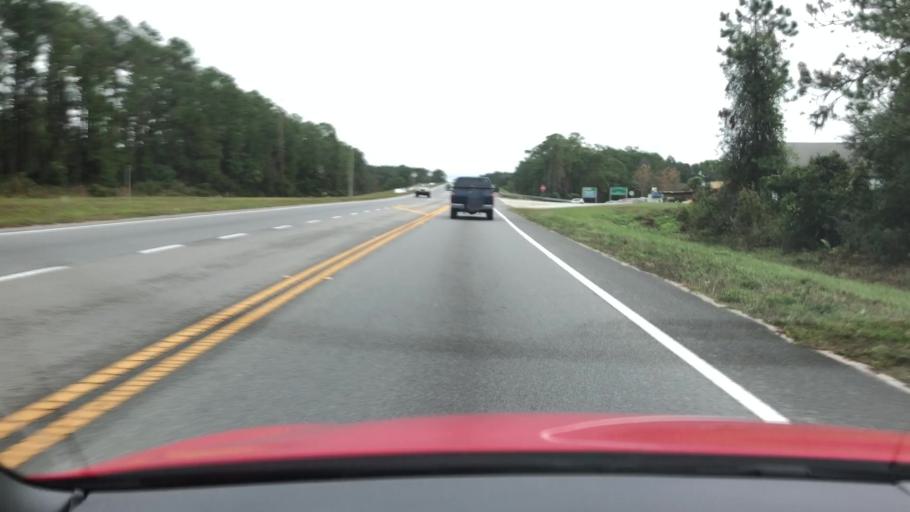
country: US
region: Florida
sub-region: Volusia County
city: West DeLand
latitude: 29.0230
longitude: -81.3598
